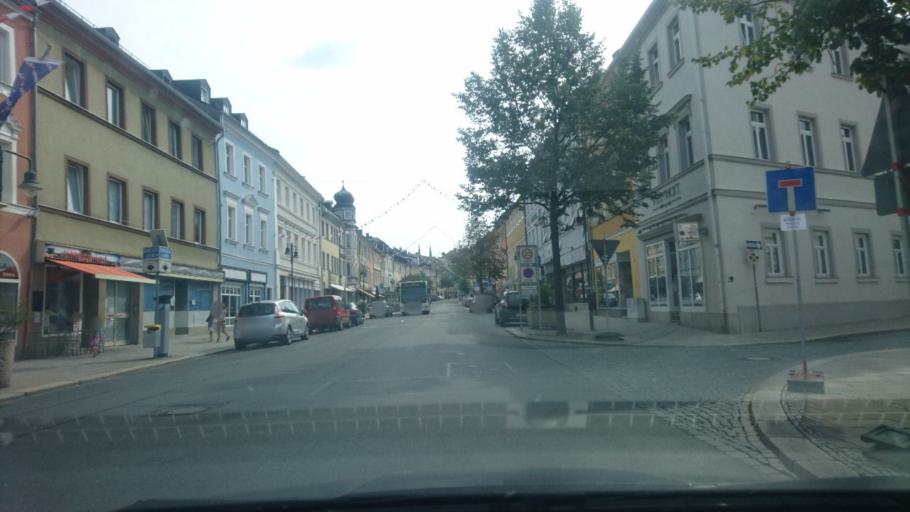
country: DE
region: Bavaria
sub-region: Upper Franconia
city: Hof
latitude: 50.3213
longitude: 11.9185
